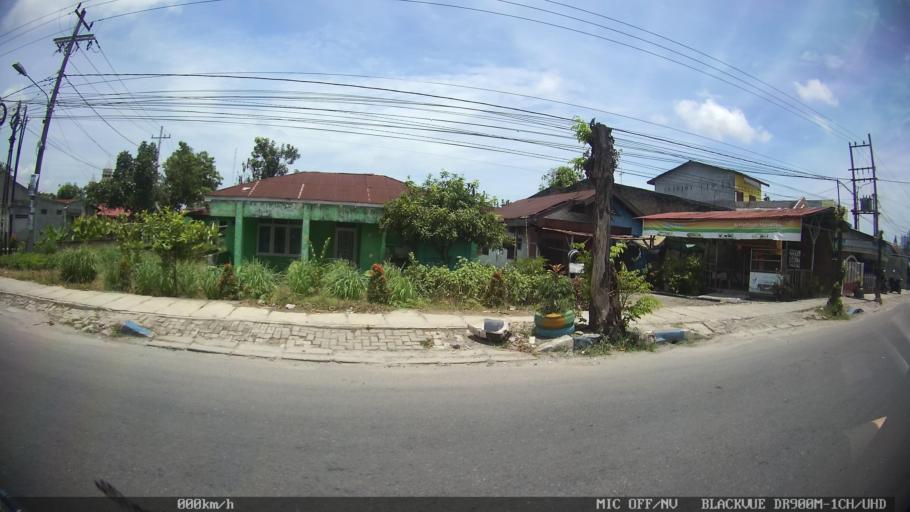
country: ID
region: North Sumatra
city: Percut
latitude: 3.5543
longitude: 98.8734
